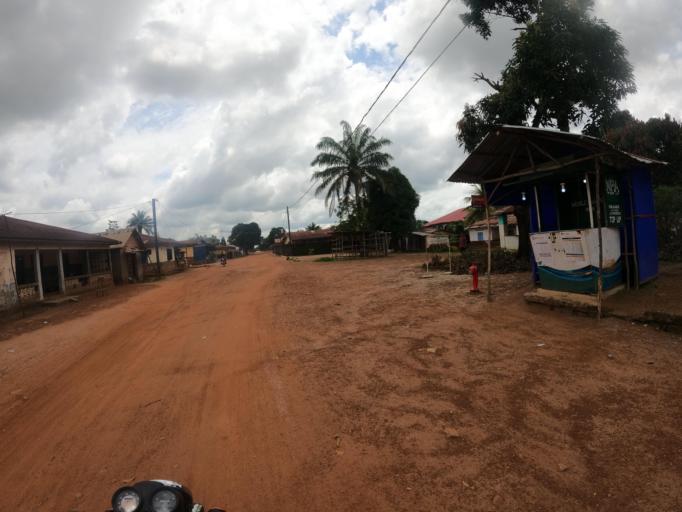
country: SL
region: Northern Province
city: Makeni
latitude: 8.9032
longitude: -12.0444
